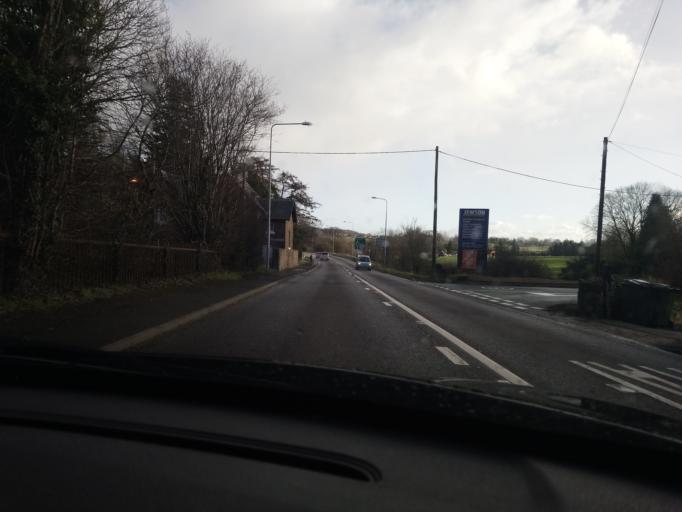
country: GB
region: Wales
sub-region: Wrexham
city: Chirk
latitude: 52.9523
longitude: -3.0624
